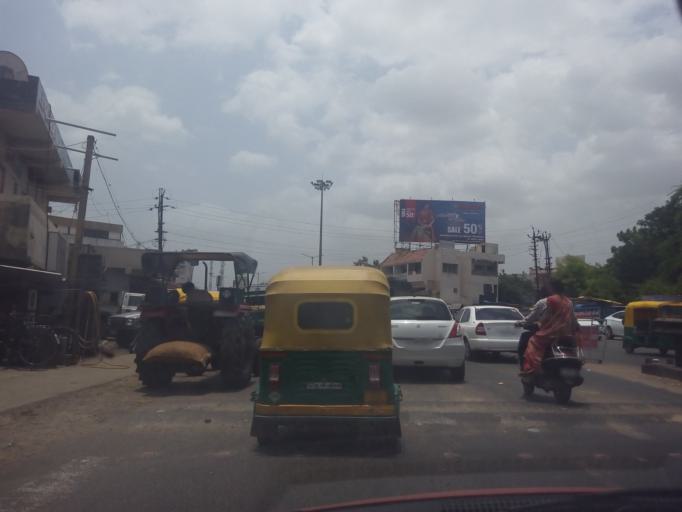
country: IN
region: Gujarat
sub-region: Ahmadabad
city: Sanand
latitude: 22.9894
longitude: 72.3807
